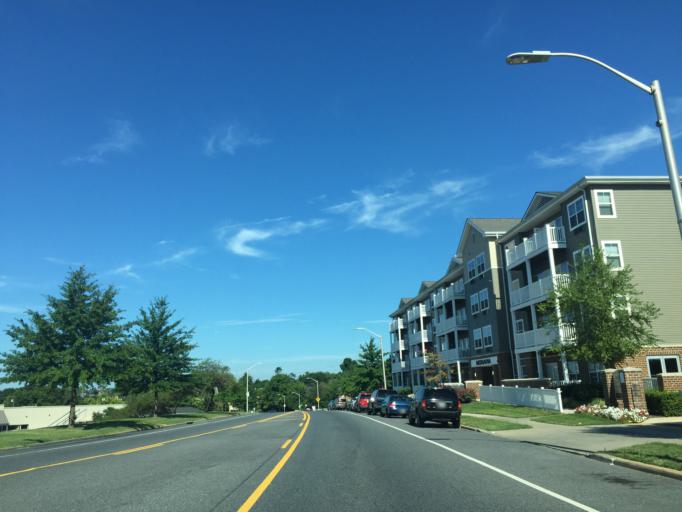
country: US
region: Maryland
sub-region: Baltimore County
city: Rosedale
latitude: 39.3156
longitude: -76.5409
